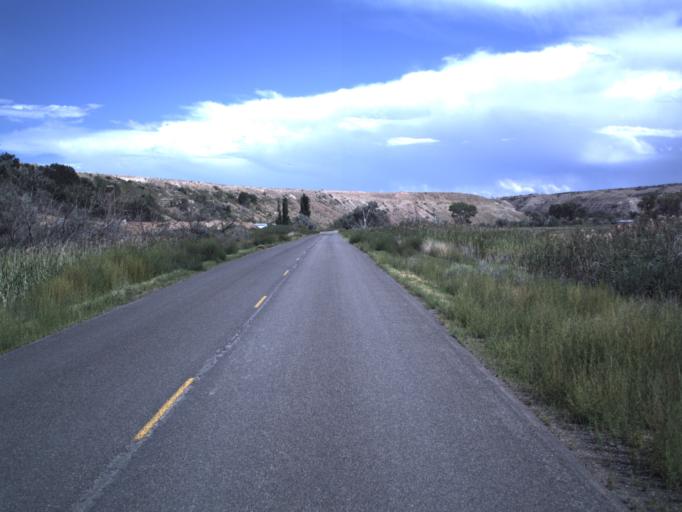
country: US
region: Utah
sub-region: Duchesne County
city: Duchesne
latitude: 40.1725
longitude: -110.4245
